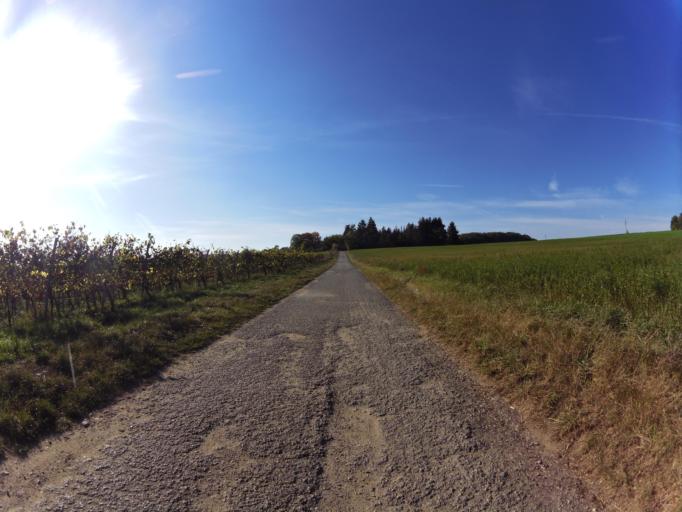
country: DE
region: Bavaria
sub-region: Regierungsbezirk Unterfranken
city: Ochsenfurt
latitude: 49.6746
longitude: 10.0660
